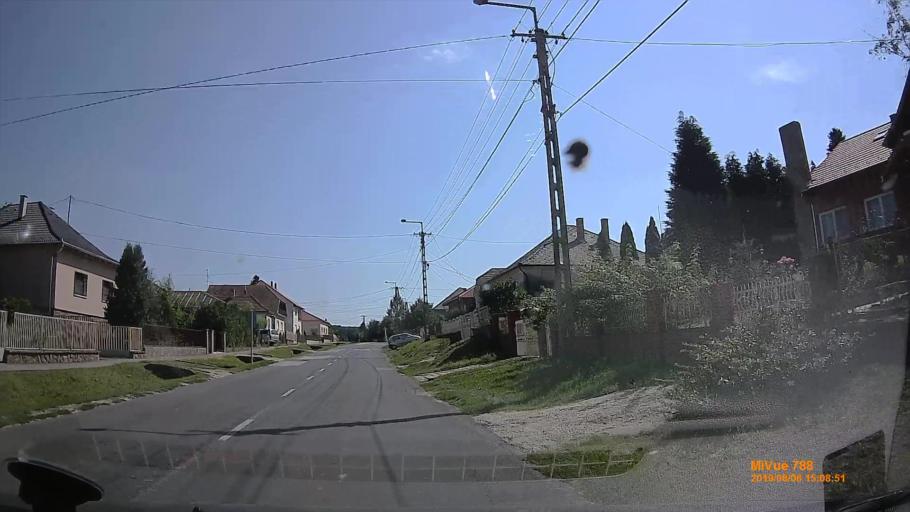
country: HU
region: Zala
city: Nagykanizsa
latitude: 46.4098
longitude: 16.9846
